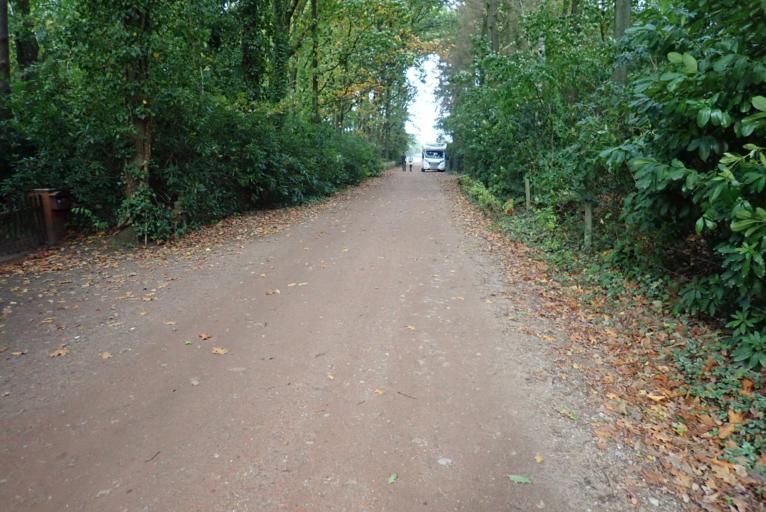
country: BE
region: Flanders
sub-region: Provincie Antwerpen
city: Essen
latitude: 51.4402
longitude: 4.4459
